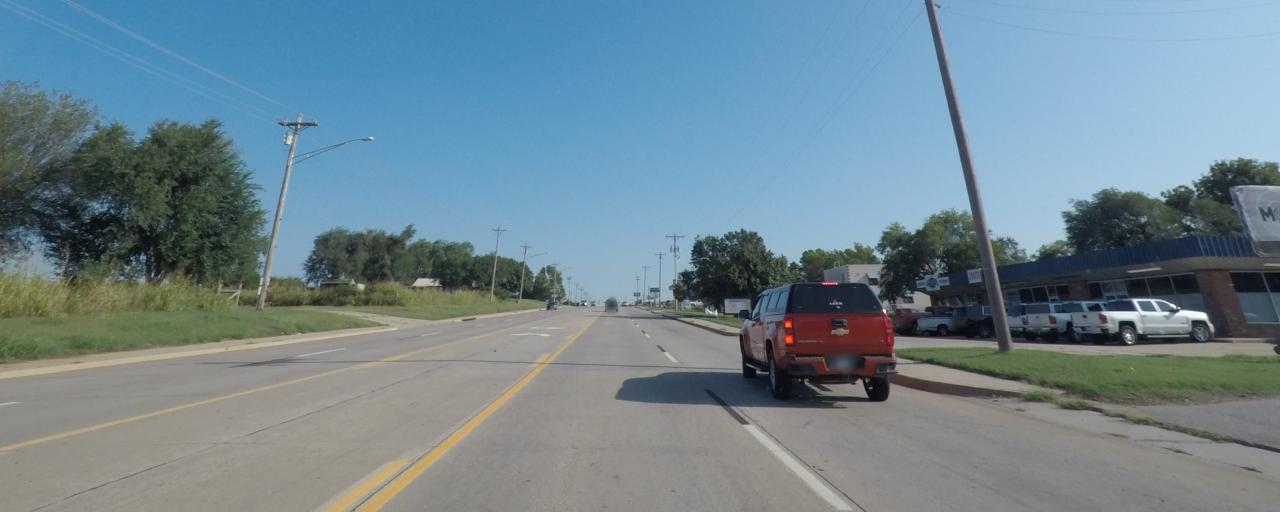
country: US
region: Oklahoma
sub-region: McClain County
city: Newcastle
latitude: 35.2521
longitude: -97.6002
